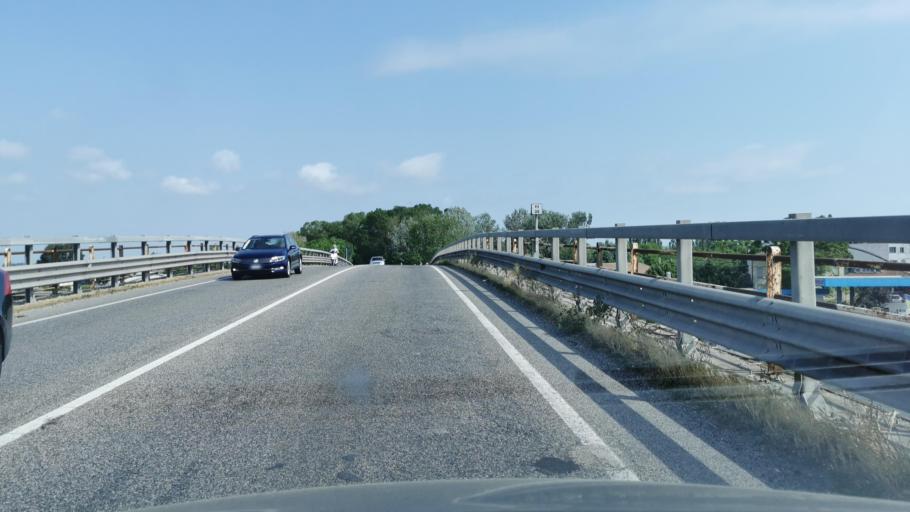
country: IT
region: Emilia-Romagna
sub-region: Provincia di Ferrara
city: Porto Garibaldi
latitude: 44.6750
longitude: 12.2281
